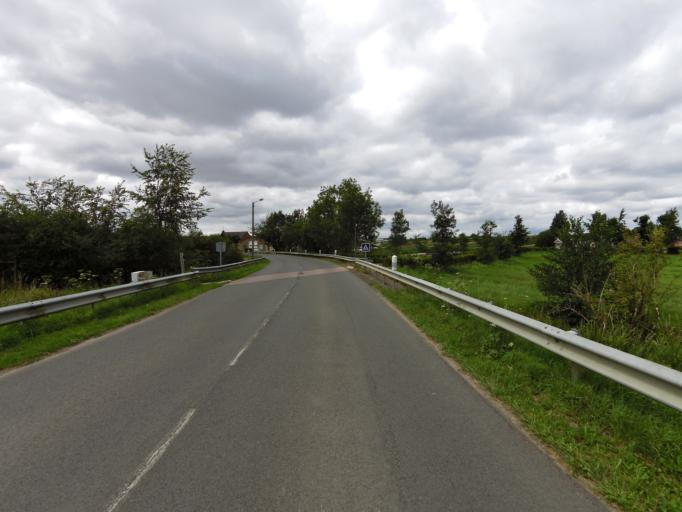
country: FR
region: Nord-Pas-de-Calais
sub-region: Departement du Nord
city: Godewaersvelde
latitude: 50.7983
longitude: 2.6498
